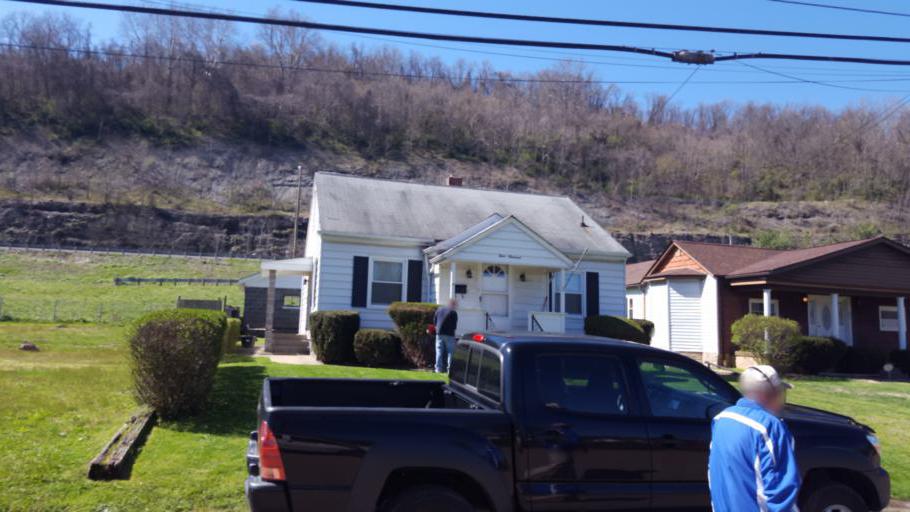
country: US
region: Ohio
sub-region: Jefferson County
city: Tiltonsville
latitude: 40.1752
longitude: -80.6972
